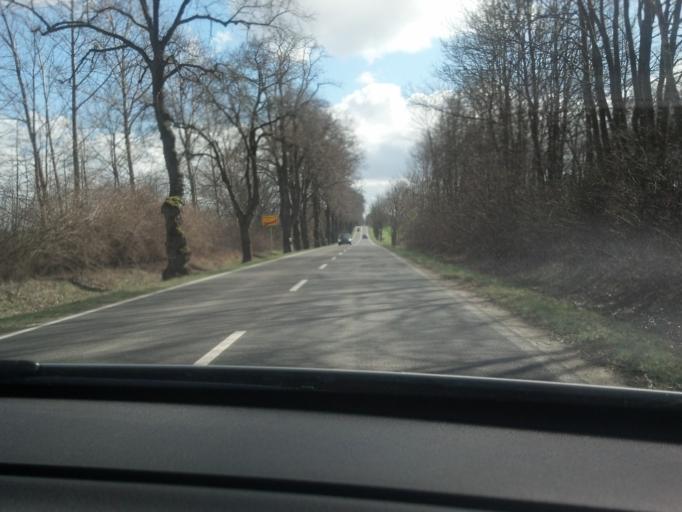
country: DE
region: Mecklenburg-Vorpommern
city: Loitz
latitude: 53.3869
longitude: 13.3418
